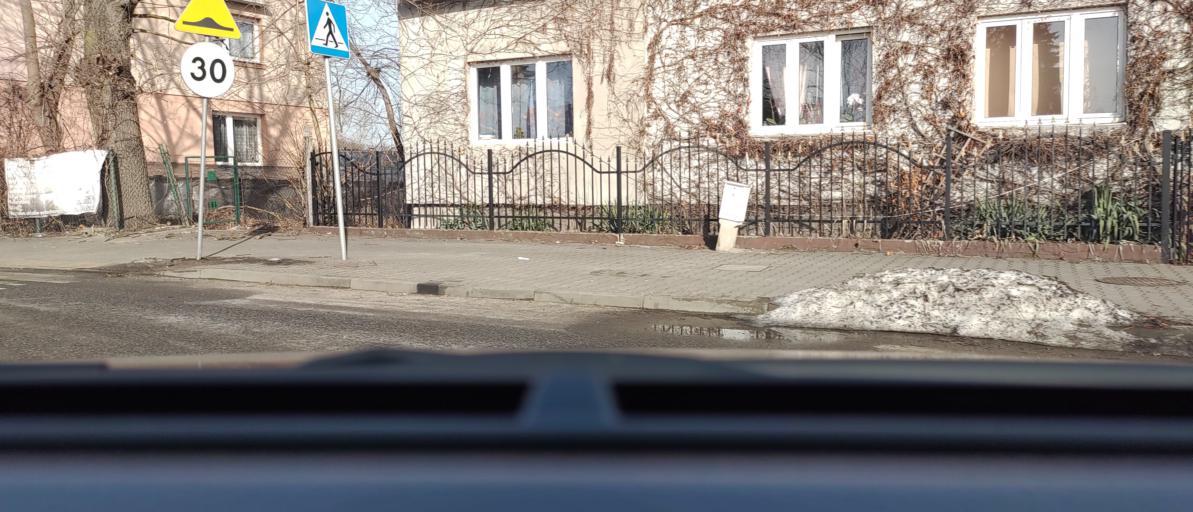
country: PL
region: Masovian Voivodeship
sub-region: Powiat bialobrzeski
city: Bialobrzegi
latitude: 51.6492
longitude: 20.9560
